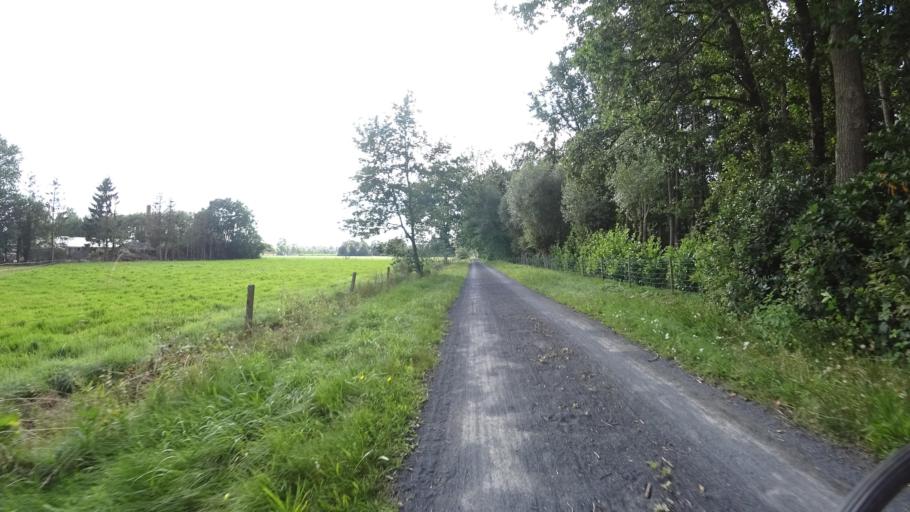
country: BE
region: Flanders
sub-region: Provincie West-Vlaanderen
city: Beernem
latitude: 51.2052
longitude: 3.3573
